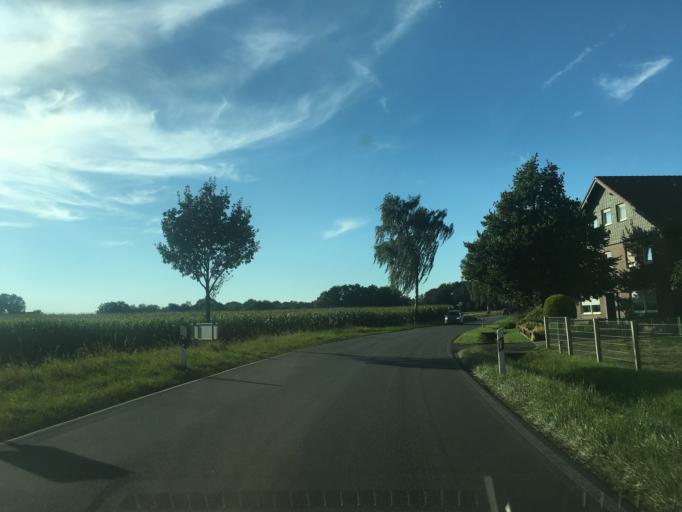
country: DE
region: North Rhine-Westphalia
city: Olfen
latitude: 51.7245
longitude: 7.3467
